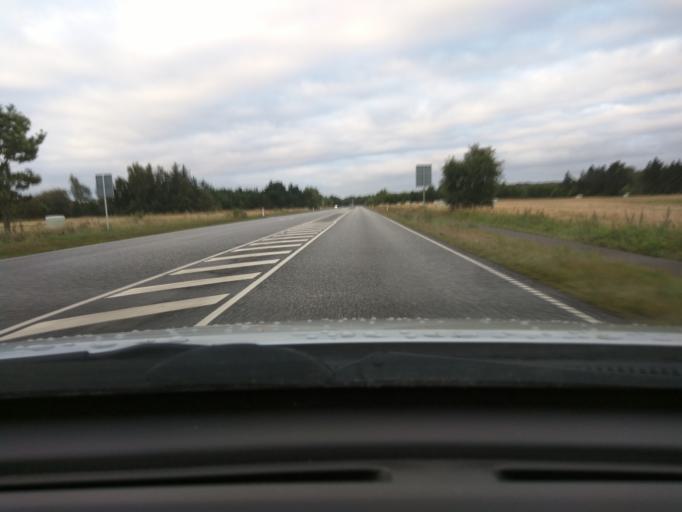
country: DK
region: Central Jutland
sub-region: Viborg Kommune
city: Viborg
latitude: 56.4120
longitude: 9.3758
